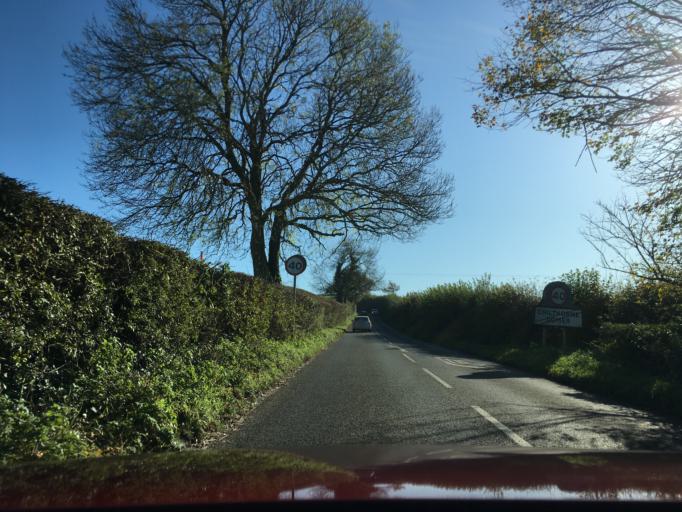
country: GB
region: England
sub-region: Somerset
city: Ilchester
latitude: 50.9633
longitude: -2.6748
